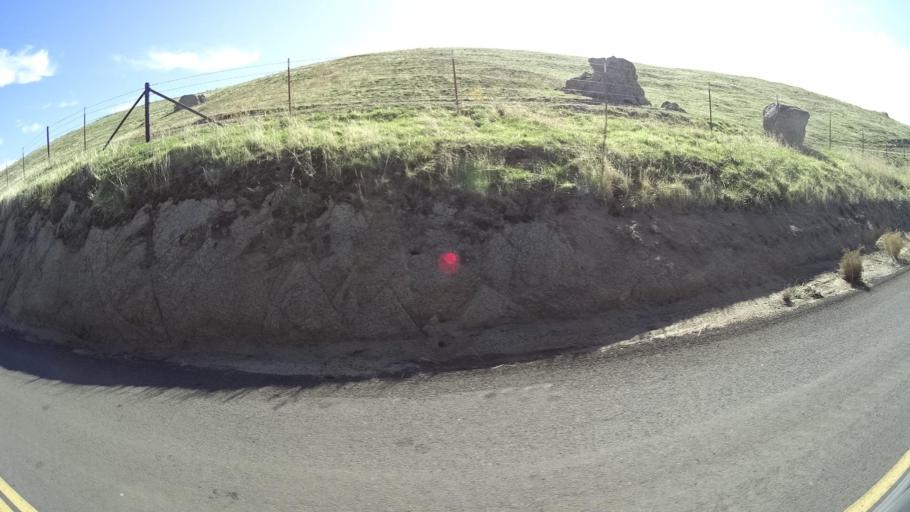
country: US
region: California
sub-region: Tulare County
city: Richgrove
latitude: 35.6833
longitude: -118.8906
